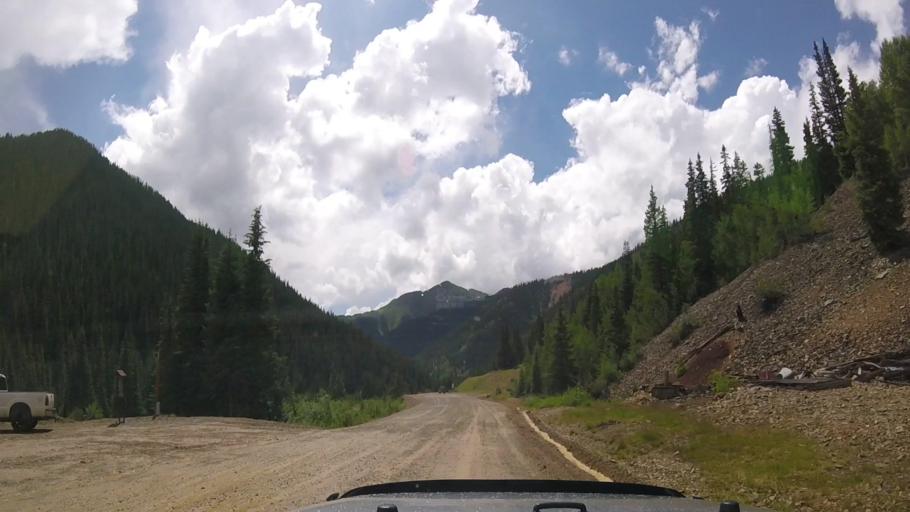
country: US
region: Colorado
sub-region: San Juan County
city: Silverton
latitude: 37.8904
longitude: -107.6523
